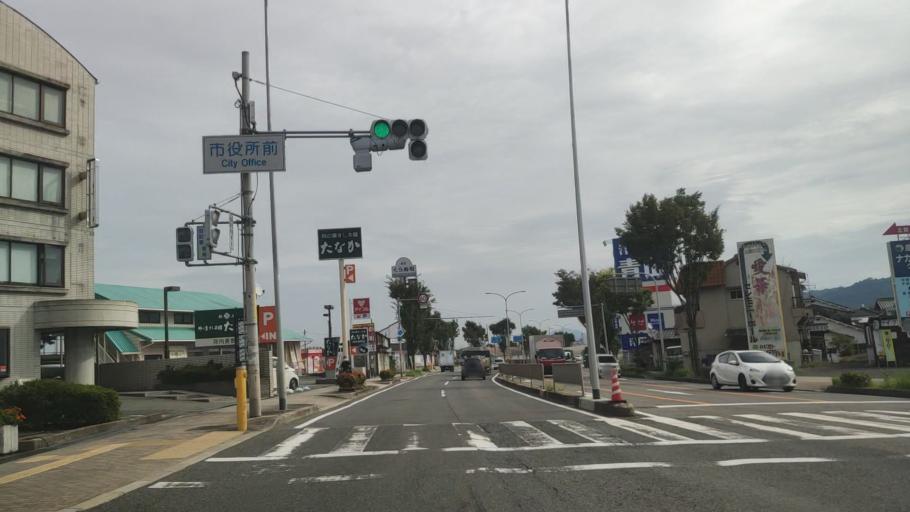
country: JP
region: Osaka
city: Tondabayashicho
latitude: 34.4567
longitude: 135.5645
